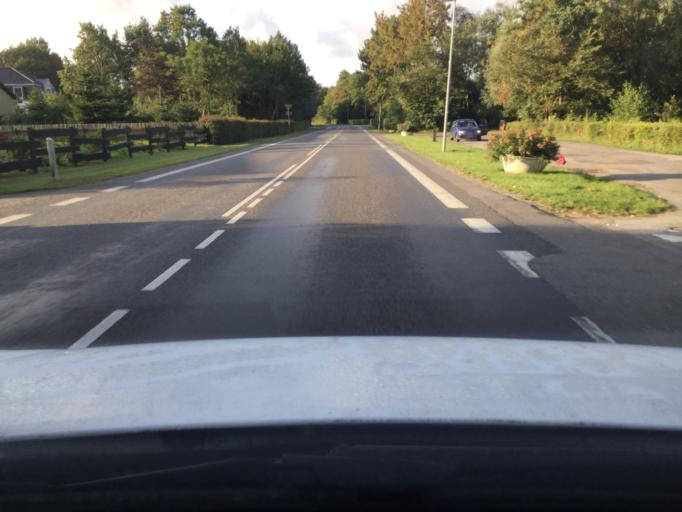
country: DK
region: Zealand
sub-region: Lolland Kommune
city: Nakskov
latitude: 54.8012
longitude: 11.2732
